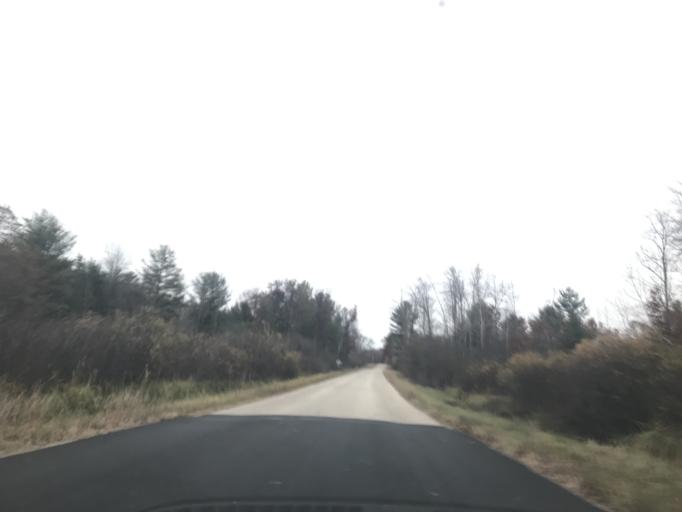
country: US
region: Wisconsin
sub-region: Marinette County
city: Peshtigo
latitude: 45.1267
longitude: -87.7499
